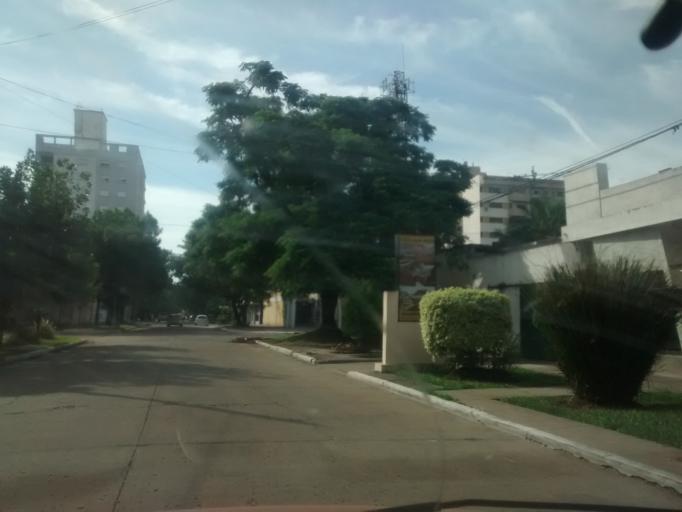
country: AR
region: Chaco
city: Resistencia
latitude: -27.4406
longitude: -58.9915
